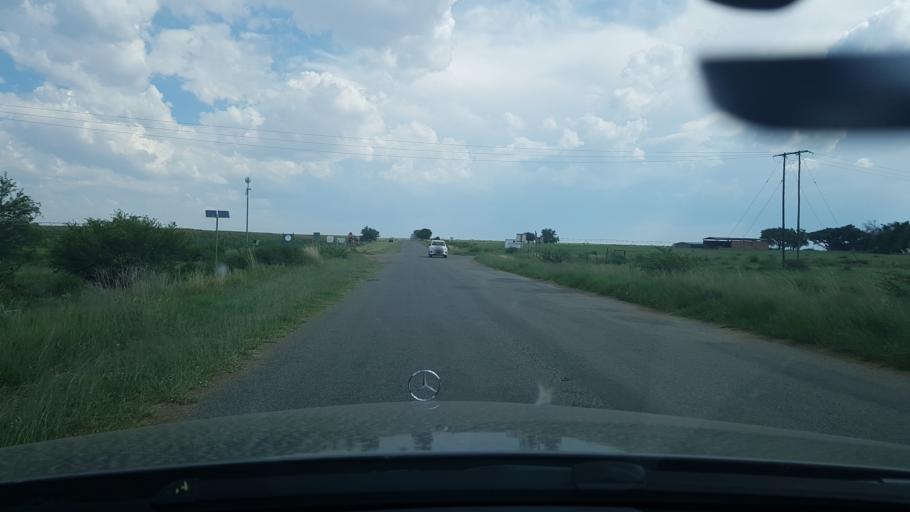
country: ZA
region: North-West
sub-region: Dr Ruth Segomotsi Mompati District Municipality
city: Bloemhof
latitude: -27.6607
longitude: 25.5935
